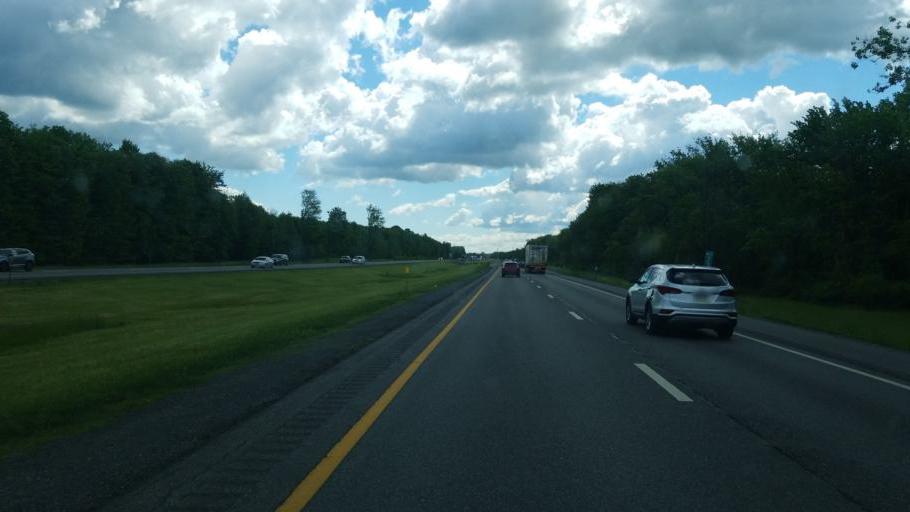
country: US
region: New York
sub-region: Madison County
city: Bolivar
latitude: 43.0915
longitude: -75.9352
